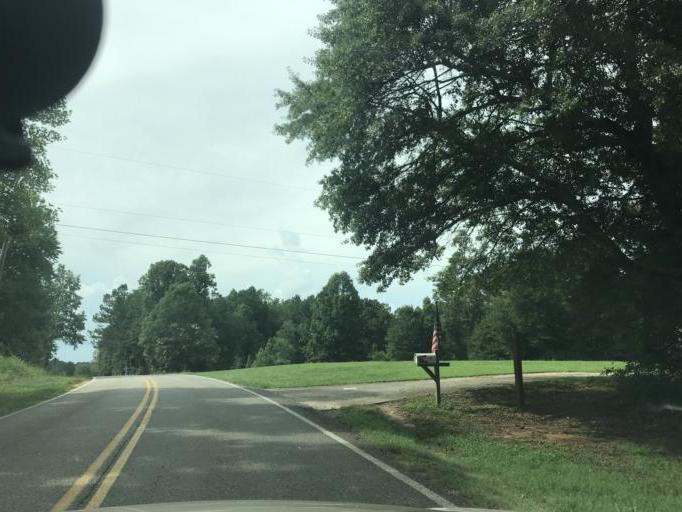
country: US
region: Georgia
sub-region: Forsyth County
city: Cumming
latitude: 34.2854
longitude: -84.2371
